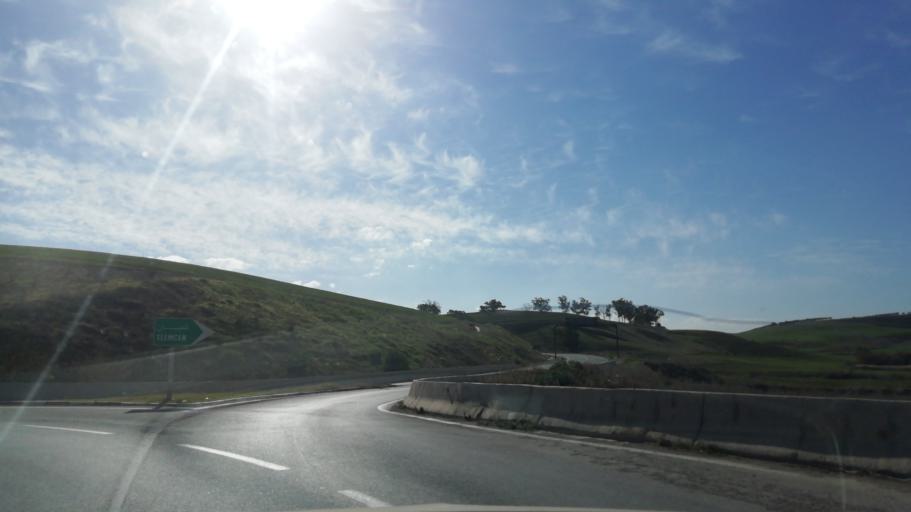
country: DZ
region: Tlemcen
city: Chetouane
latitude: 34.9809
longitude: -1.2375
